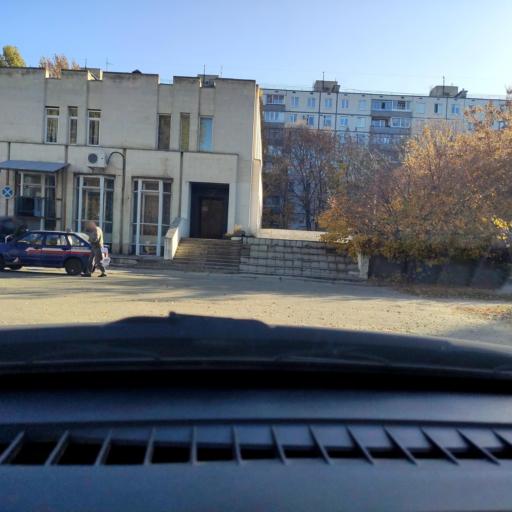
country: RU
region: Samara
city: Tol'yatti
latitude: 53.5113
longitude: 49.2780
